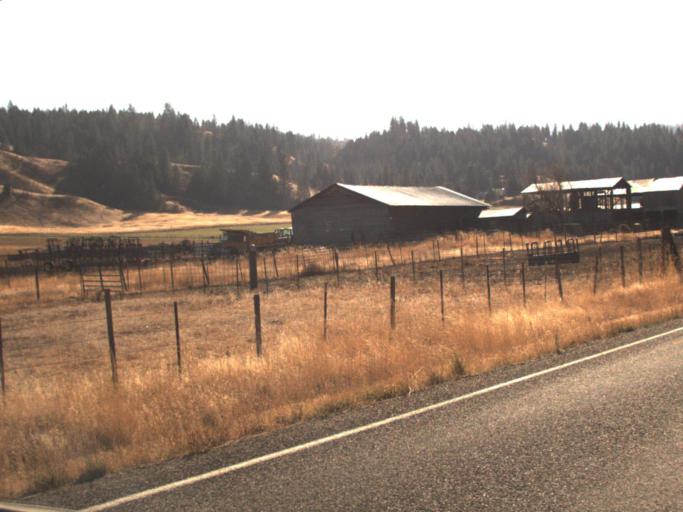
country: US
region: Washington
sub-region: Ferry County
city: Republic
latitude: 48.8147
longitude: -118.5995
